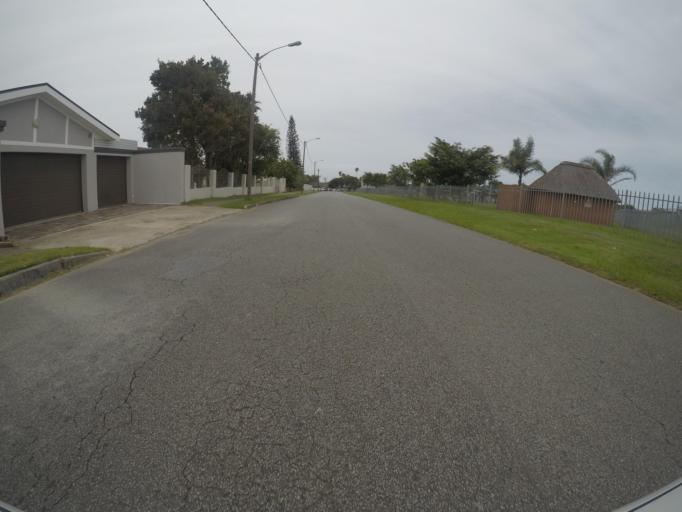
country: ZA
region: Eastern Cape
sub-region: Buffalo City Metropolitan Municipality
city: East London
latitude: -32.9666
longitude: 27.9367
